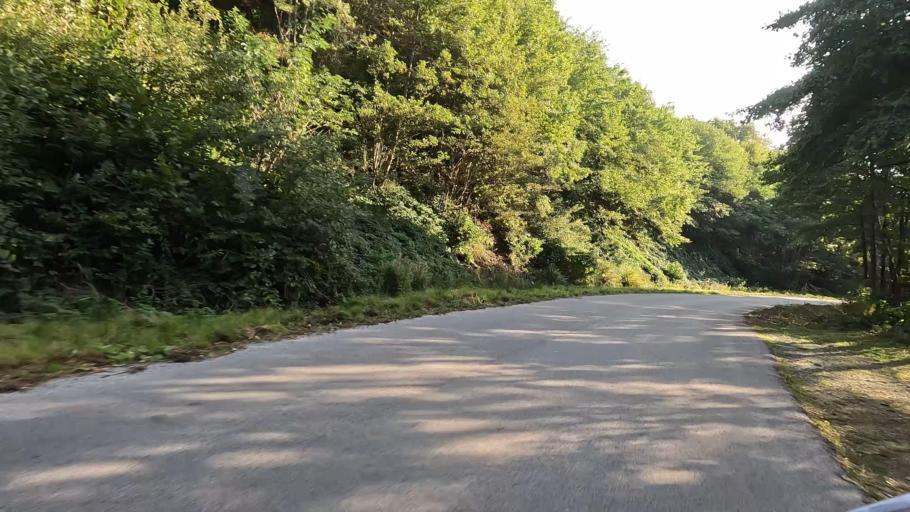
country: IT
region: Liguria
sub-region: Provincia di Savona
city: San Giovanni
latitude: 44.4184
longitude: 8.5307
